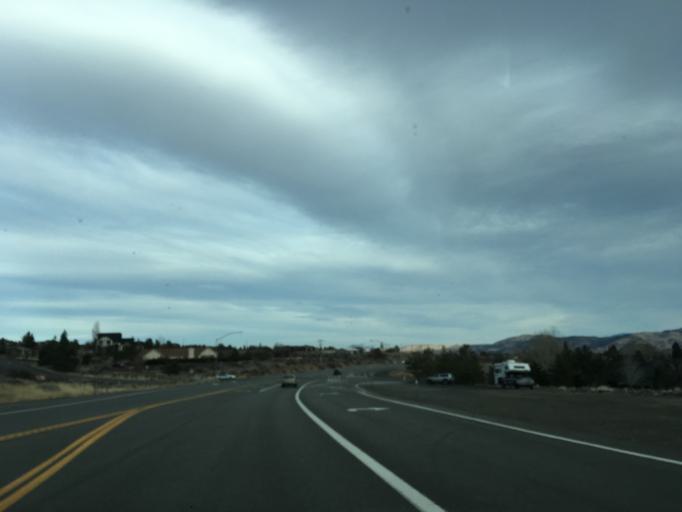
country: US
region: Nevada
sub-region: Washoe County
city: Reno
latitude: 39.3754
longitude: -119.8408
